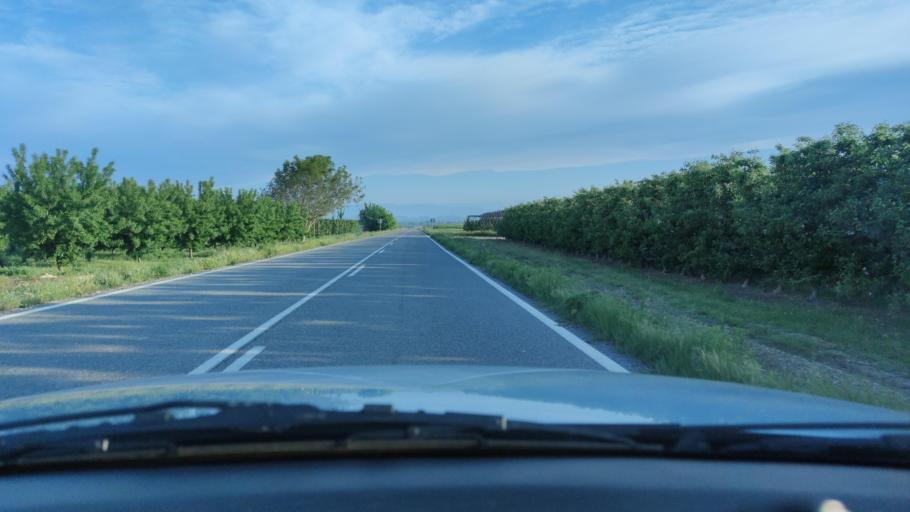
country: ES
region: Catalonia
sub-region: Provincia de Lleida
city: Ivars d'Urgell
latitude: 41.6941
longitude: 0.9859
